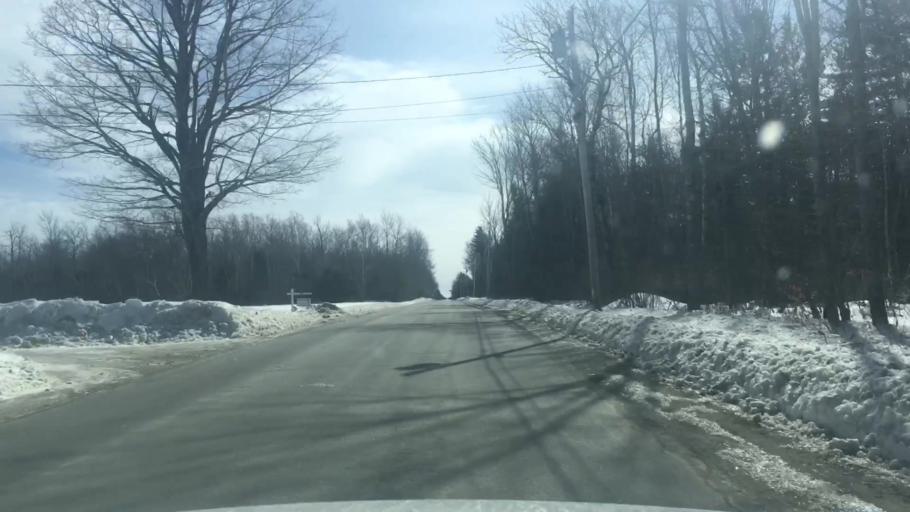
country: US
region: Maine
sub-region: Penobscot County
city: Holden
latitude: 44.7737
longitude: -68.6501
